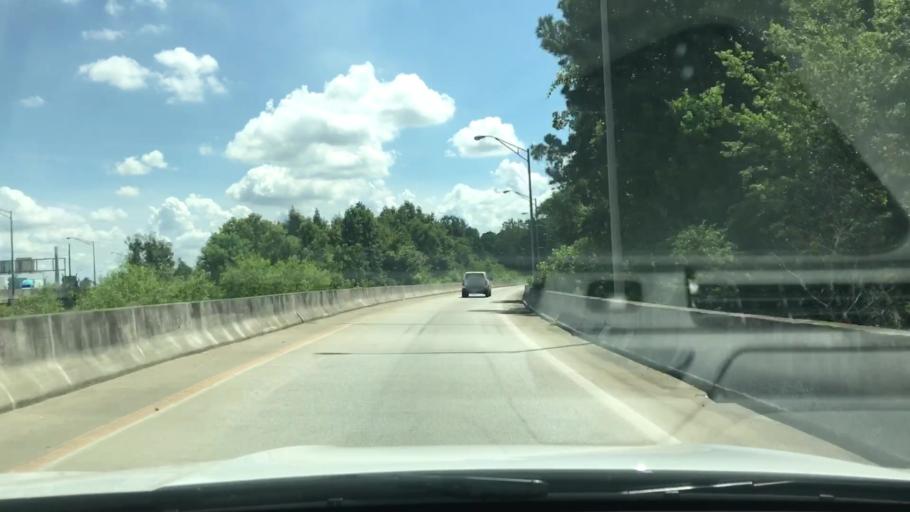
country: US
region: South Carolina
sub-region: Berkeley County
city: Hanahan
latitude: 32.8940
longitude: -79.9907
